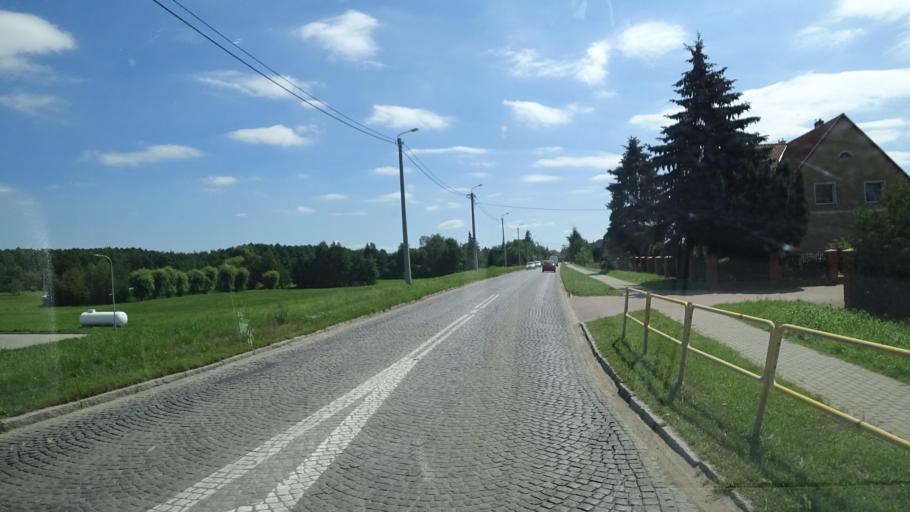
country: PL
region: Warmian-Masurian Voivodeship
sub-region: Powiat elcki
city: Prostki
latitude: 53.6935
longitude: 22.4417
